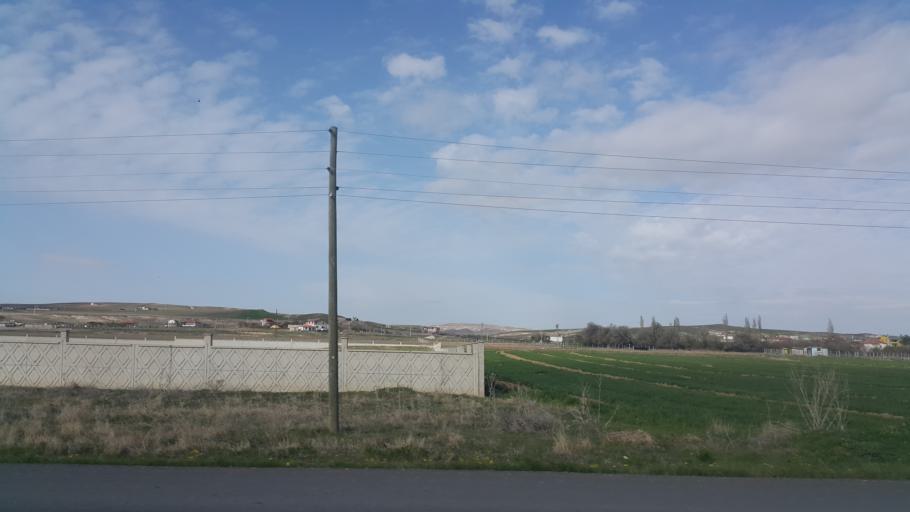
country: TR
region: Aksaray
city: Aksaray
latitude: 38.4262
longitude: 33.9581
